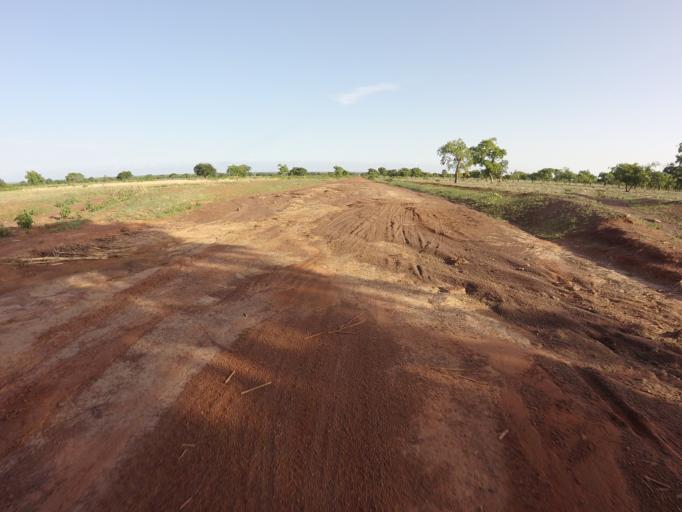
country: TG
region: Savanes
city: Sansanne-Mango
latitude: 10.3825
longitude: -0.0948
